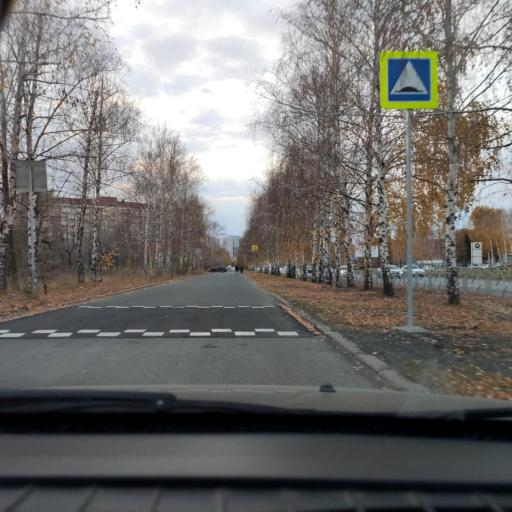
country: RU
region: Samara
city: Tol'yatti
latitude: 53.5013
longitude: 49.2635
